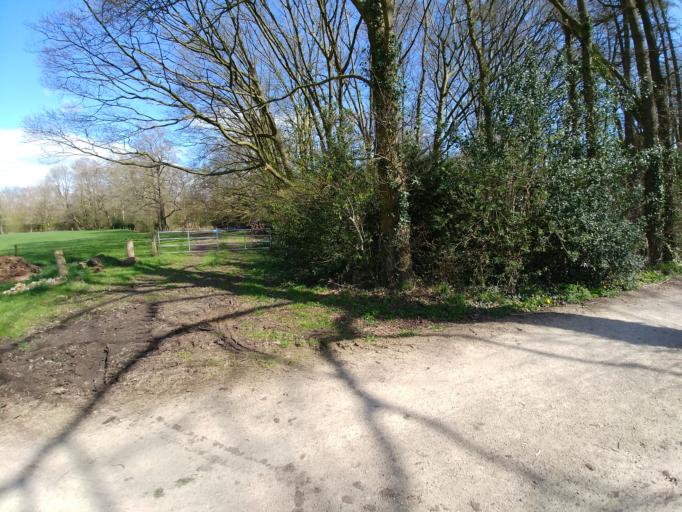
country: NL
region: Overijssel
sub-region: Gemeente Olst-Wijhe
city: Boskamp
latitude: 52.2947
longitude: 6.1293
